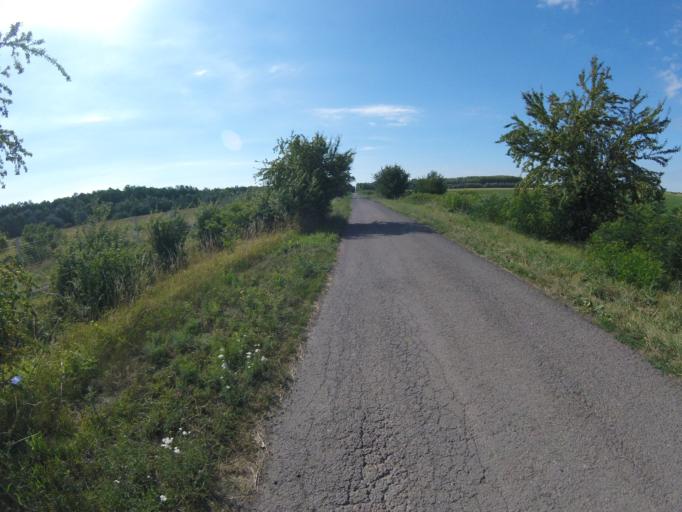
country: HU
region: Heves
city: Tiszanana
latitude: 47.5785
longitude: 20.6050
